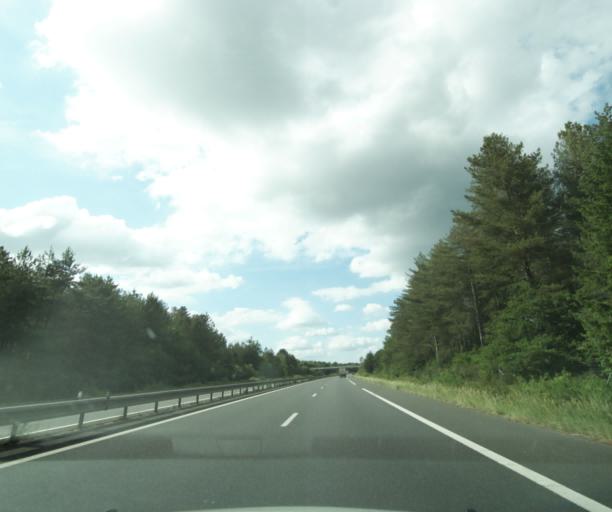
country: FR
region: Centre
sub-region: Departement du Loir-et-Cher
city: Lamotte-Beuvron
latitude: 47.6091
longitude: 1.9681
